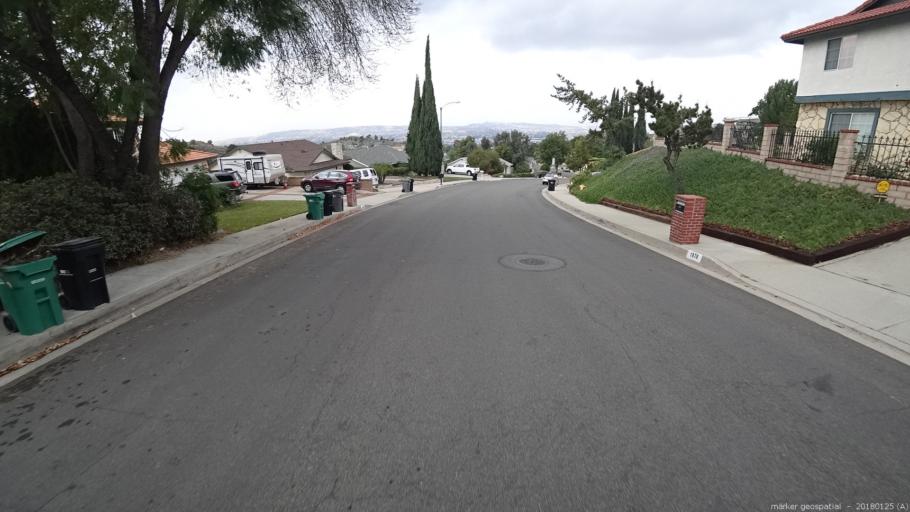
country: US
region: California
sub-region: Los Angeles County
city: Walnut
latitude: 33.9869
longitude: -117.8414
